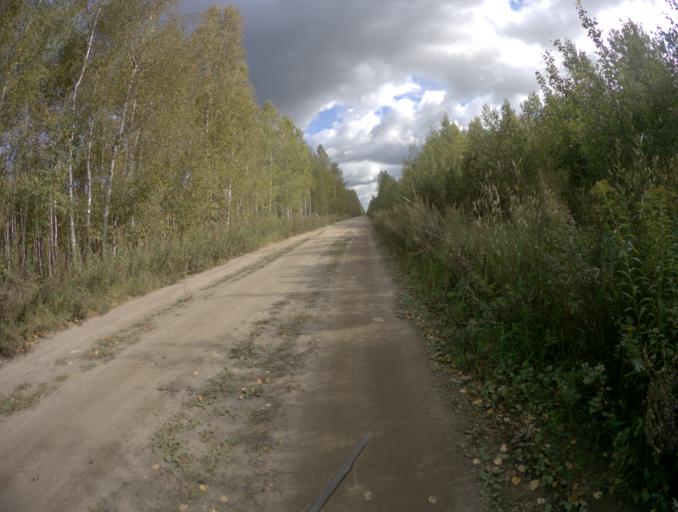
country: RU
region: Moskovskaya
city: Baksheyevo
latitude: 55.7144
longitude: 39.9083
